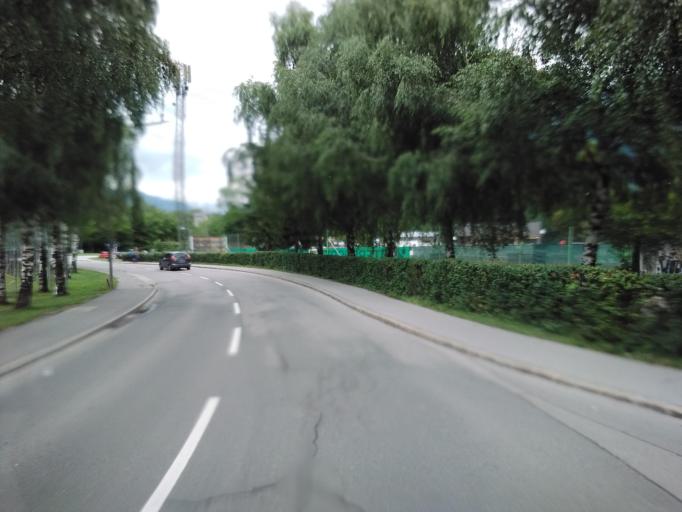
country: AT
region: Tyrol
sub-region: Politischer Bezirk Lienz
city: Lienz
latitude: 46.8248
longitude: 12.7684
